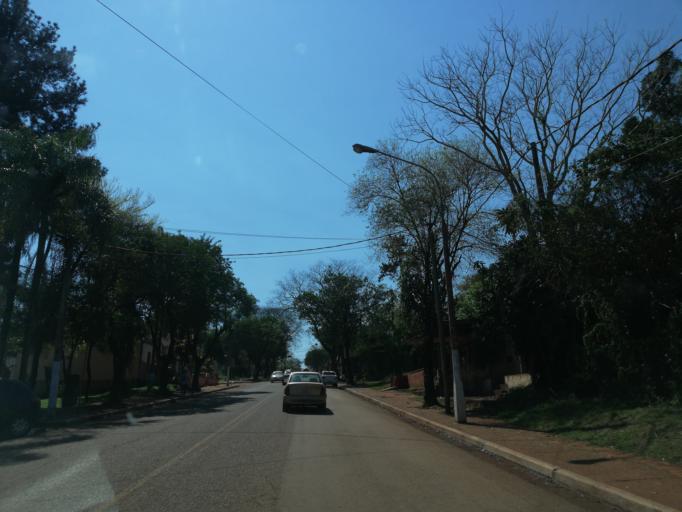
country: AR
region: Misiones
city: Puerto Eldorado
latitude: -26.4084
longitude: -54.6721
